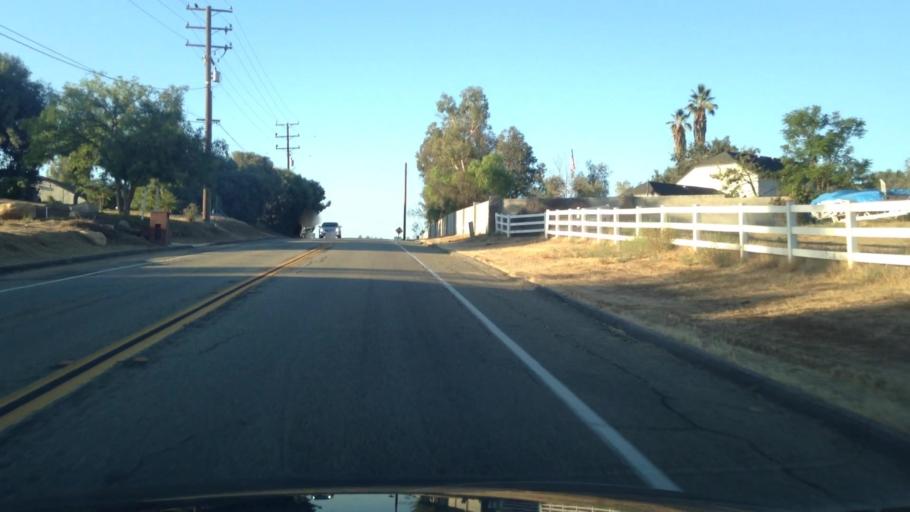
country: US
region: California
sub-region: Riverside County
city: Woodcrest
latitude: 33.8486
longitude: -117.3747
